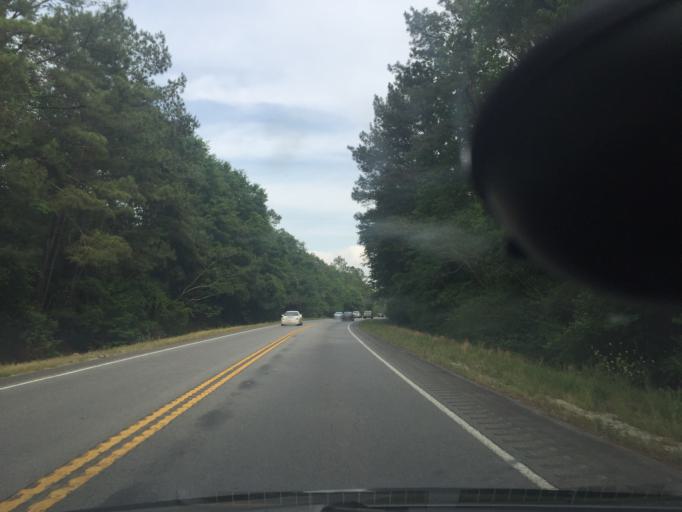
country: US
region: Georgia
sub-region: Bryan County
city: Richmond Hill
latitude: 32.0160
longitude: -81.3032
